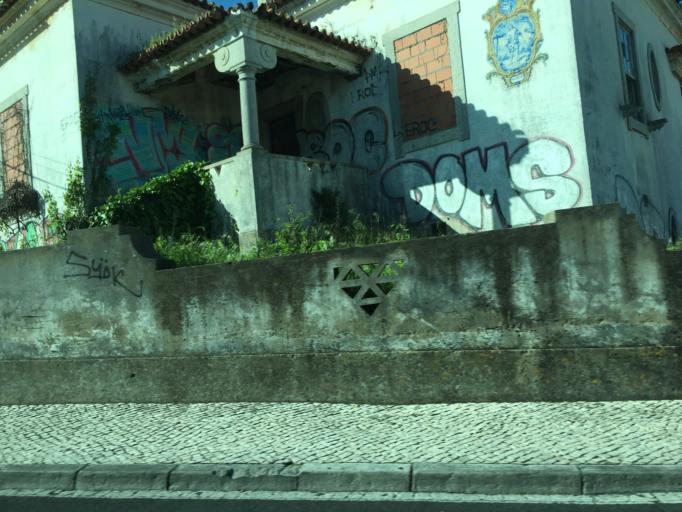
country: PT
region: Lisbon
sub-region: Cascais
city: Estoril
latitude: 38.7028
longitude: -9.3907
